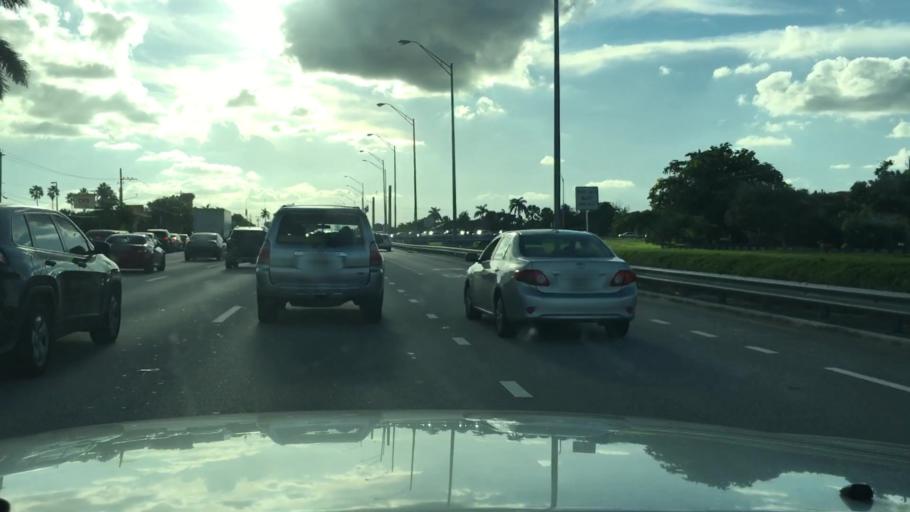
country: US
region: Florida
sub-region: Miami-Dade County
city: Tamiami
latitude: 25.7605
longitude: -80.3913
